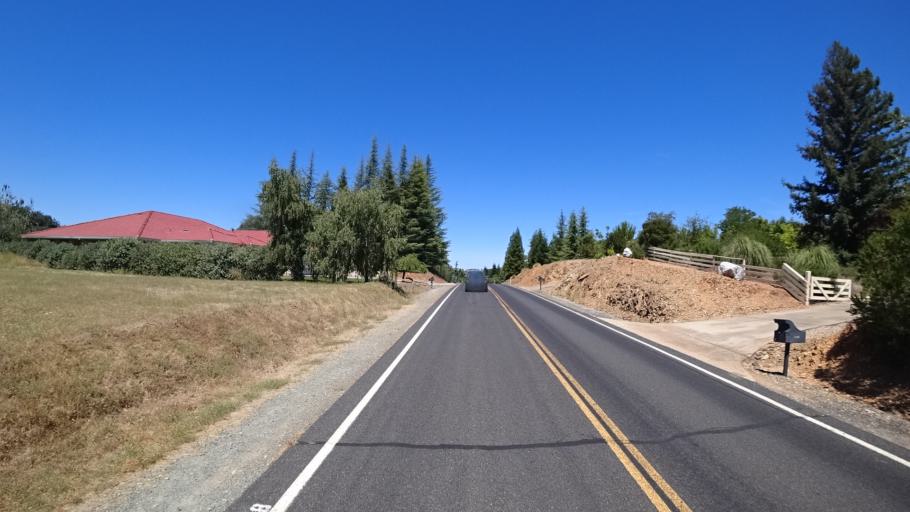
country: US
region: California
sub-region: Calaveras County
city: Valley Springs
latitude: 38.1633
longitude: -120.8280
